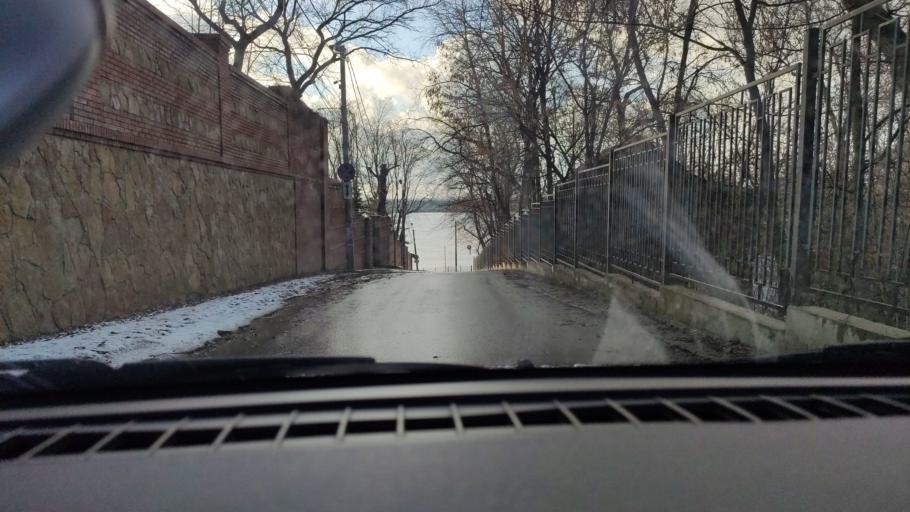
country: RU
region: Samara
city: Samara
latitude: 53.2632
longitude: 50.1844
